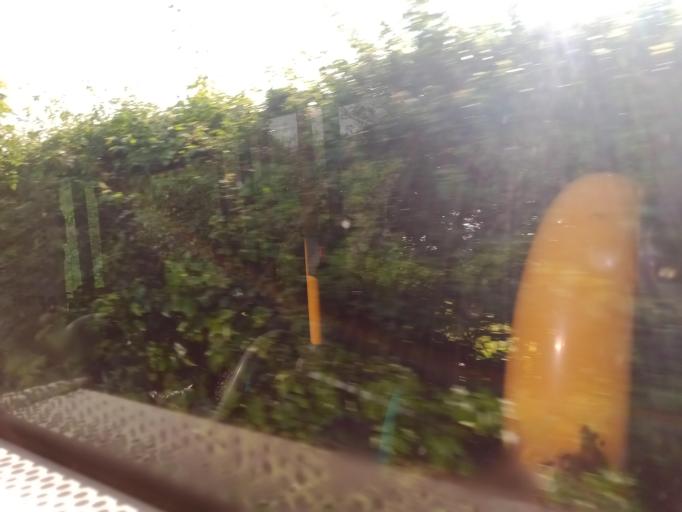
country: GB
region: Wales
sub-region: Anglesey
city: Llangoed
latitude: 53.3024
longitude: -4.0846
